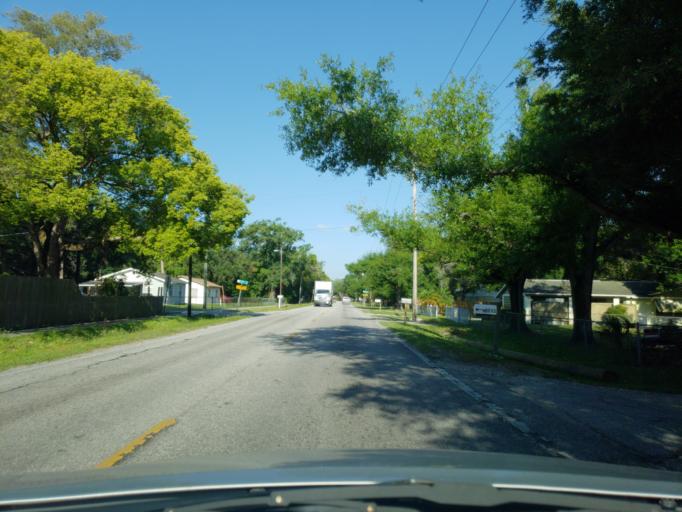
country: US
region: Florida
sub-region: Hillsborough County
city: Palm River-Clair Mel
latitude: 27.9432
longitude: -82.3913
